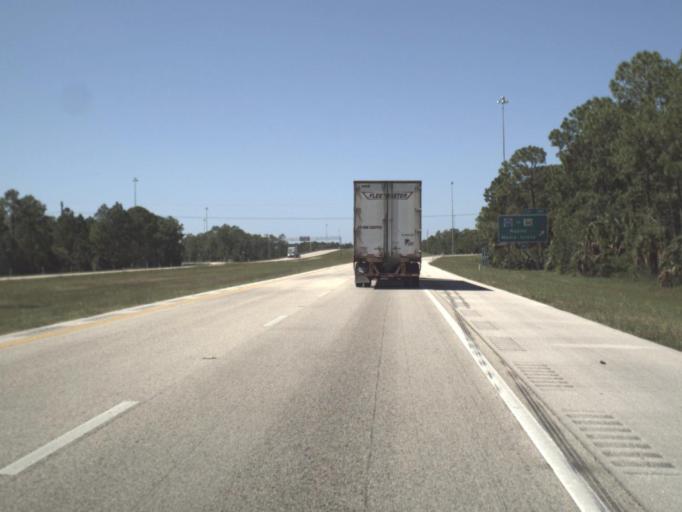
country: US
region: Florida
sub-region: Collier County
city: Golden Gate
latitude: 26.1585
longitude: -81.6789
